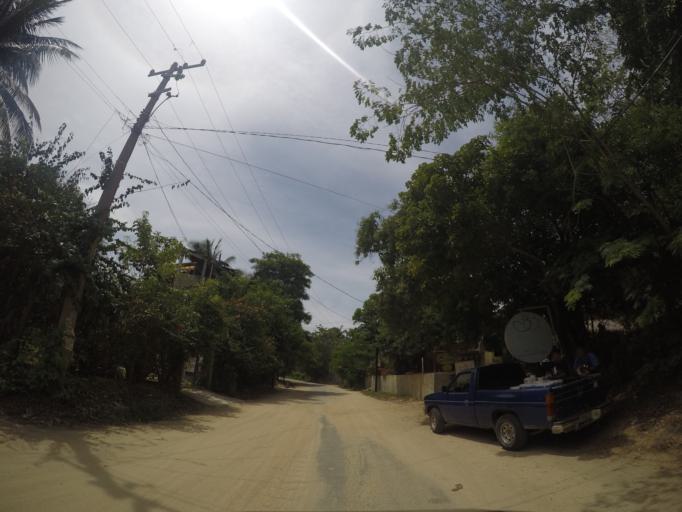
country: MX
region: Oaxaca
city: Santa Maria Tonameca
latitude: 15.6649
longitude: -96.5155
